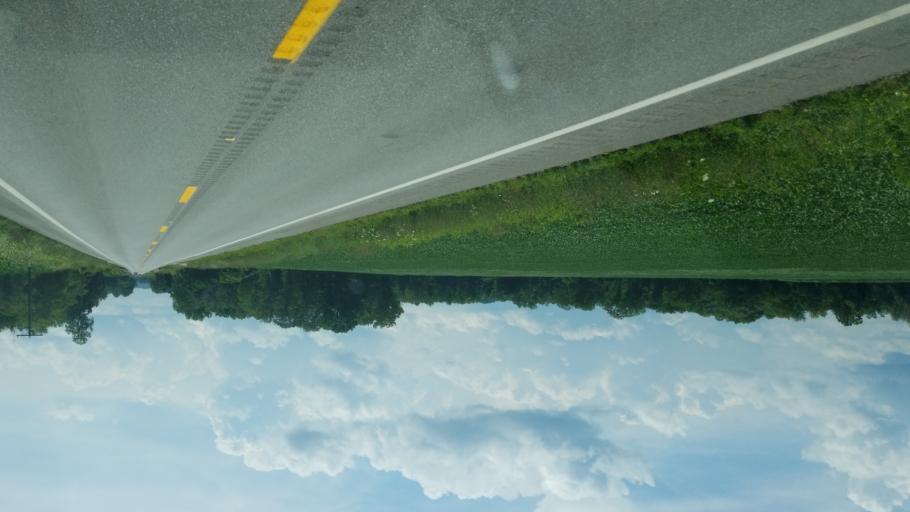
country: US
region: West Virginia
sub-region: Putnam County
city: Buffalo
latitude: 38.6933
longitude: -81.9656
